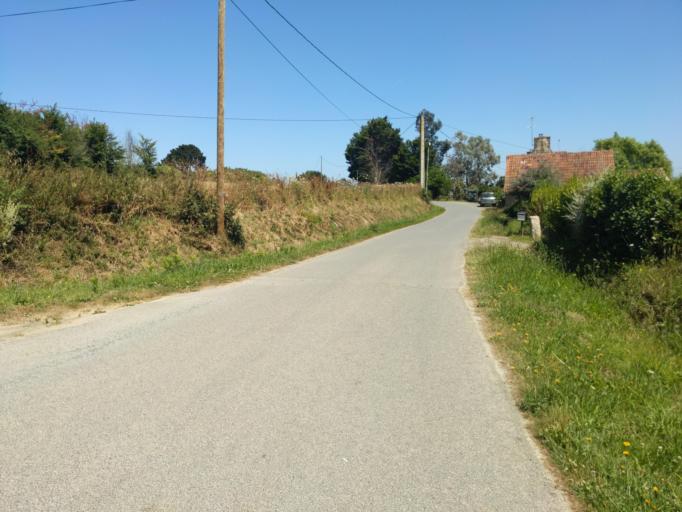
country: FR
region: Brittany
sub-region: Departement des Cotes-d'Armor
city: Plouguiel
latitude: 48.8108
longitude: -3.2158
